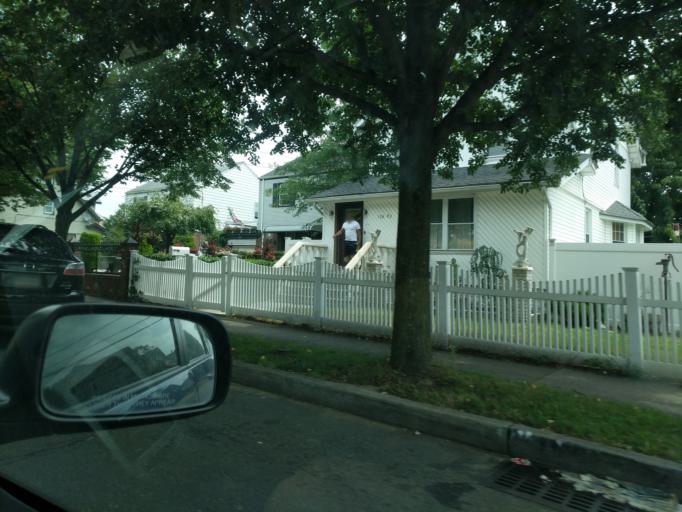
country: US
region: New York
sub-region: Nassau County
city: South Valley Stream
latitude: 40.6677
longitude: -73.7295
